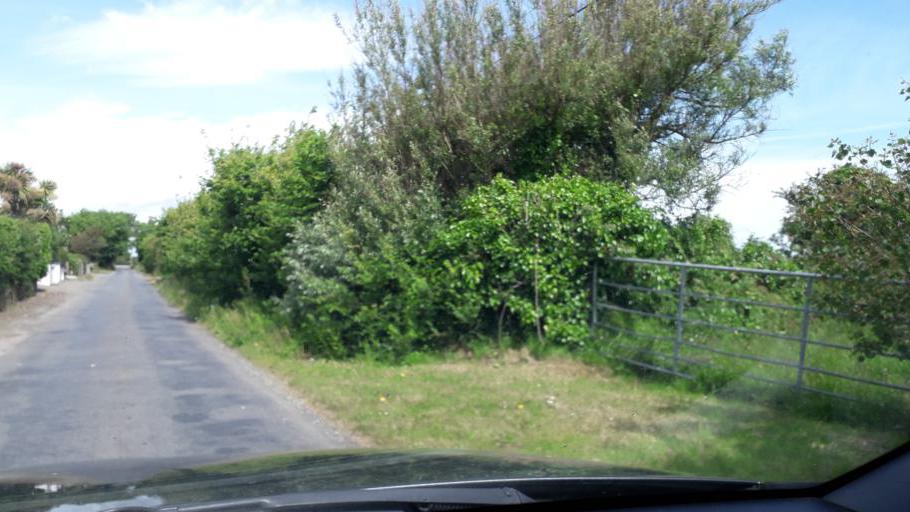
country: IE
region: Leinster
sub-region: Loch Garman
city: Loch Garman
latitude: 52.1916
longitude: -6.5459
